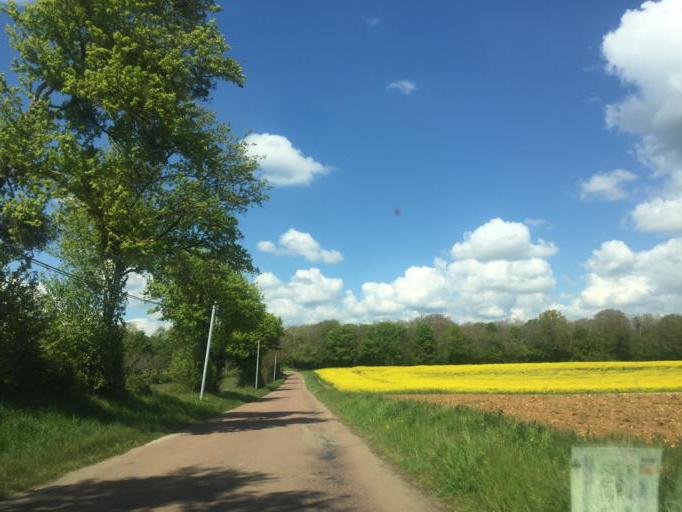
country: FR
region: Bourgogne
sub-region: Departement de l'Yonne
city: Fontenailles
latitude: 47.4961
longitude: 3.3702
